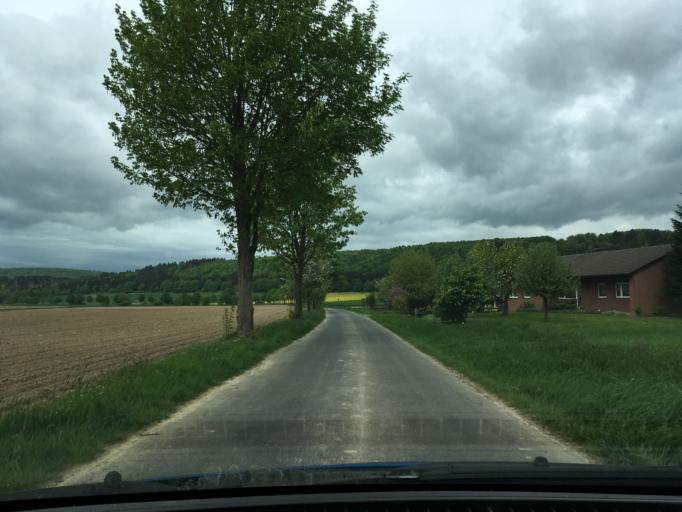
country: DE
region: Lower Saxony
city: Bodenfelde
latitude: 51.6515
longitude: 9.5380
